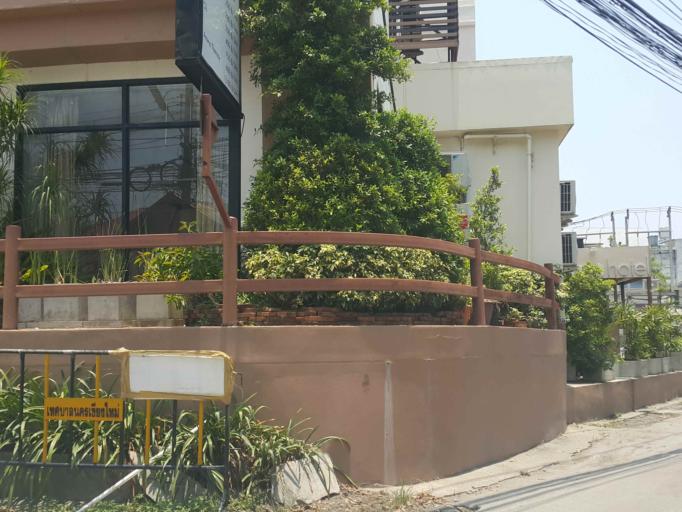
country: TH
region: Chiang Mai
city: Chiang Mai
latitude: 18.7867
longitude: 98.9941
